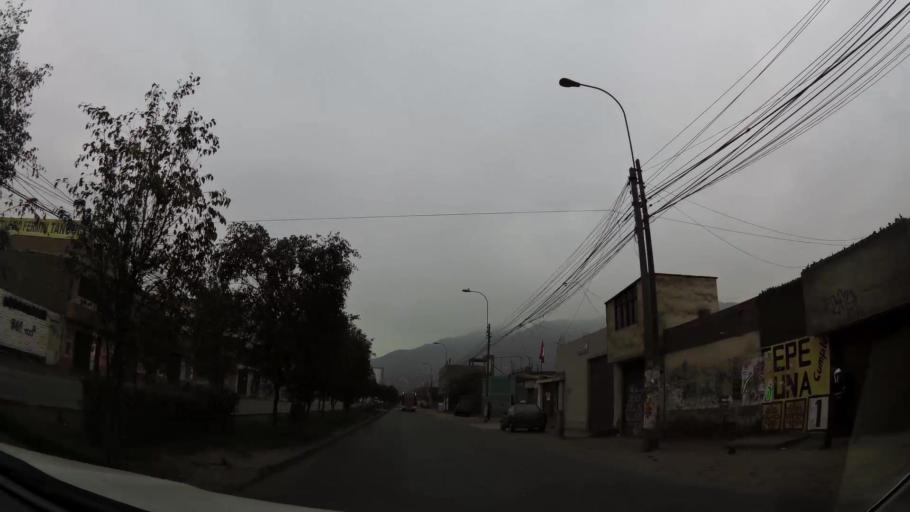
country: PE
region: Lima
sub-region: Lima
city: Independencia
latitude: -11.9778
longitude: -77.0105
